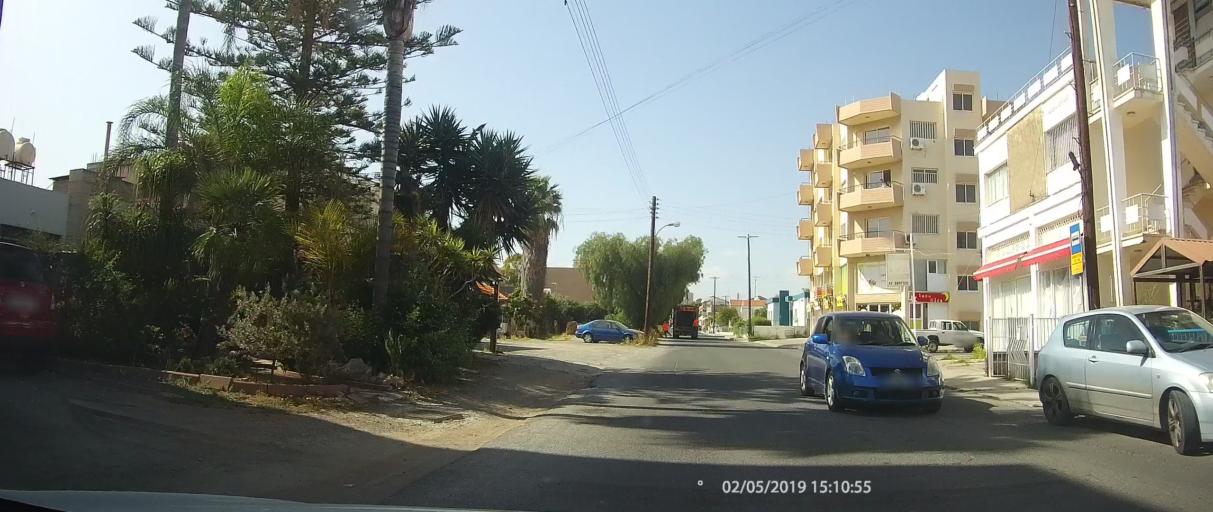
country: CY
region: Limassol
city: Limassol
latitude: 34.6708
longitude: 33.0229
